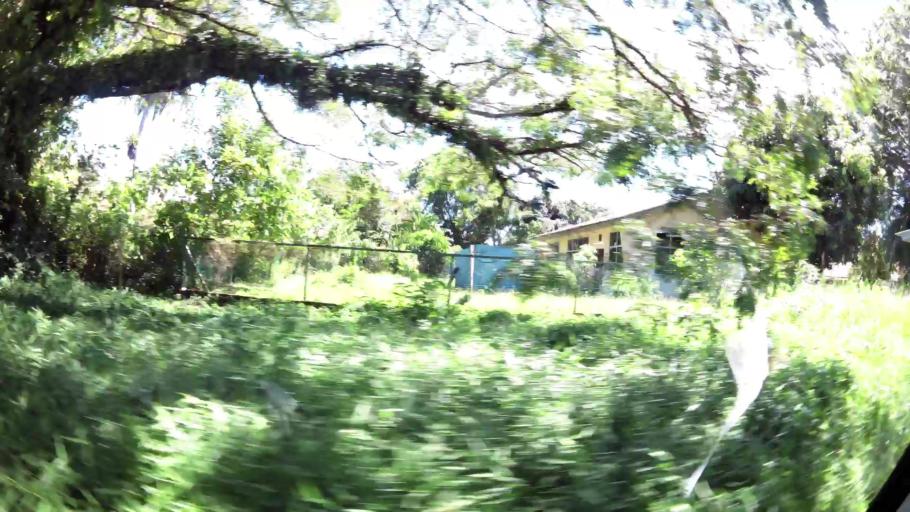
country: BN
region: Brunei and Muara
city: Bandar Seri Begawan
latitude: 5.0321
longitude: 115.0683
